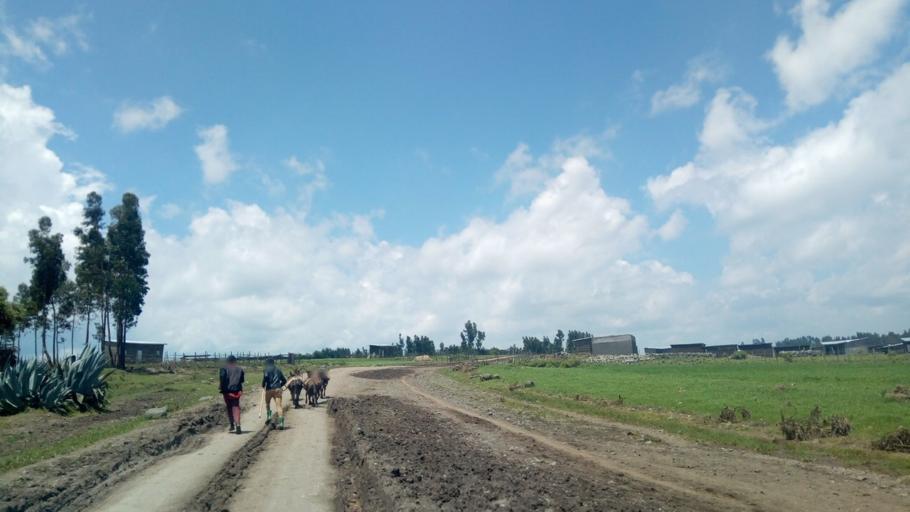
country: ET
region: Oromiya
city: Sendafa
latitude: 8.9755
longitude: 39.1197
